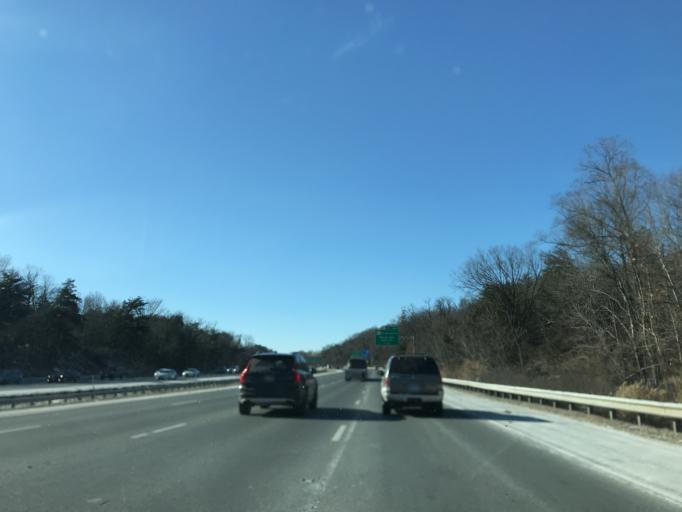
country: US
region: Maryland
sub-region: Prince George's County
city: Temple Hills
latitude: 38.8153
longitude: -76.9550
